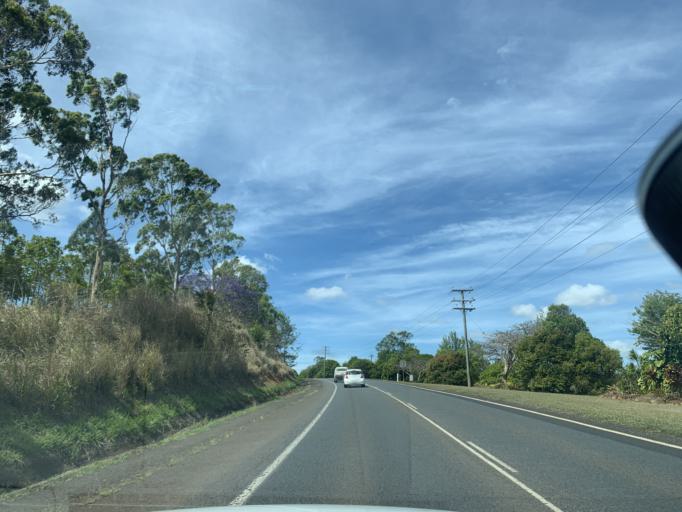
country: AU
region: Queensland
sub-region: Tablelands
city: Atherton
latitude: -17.2514
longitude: 145.4781
